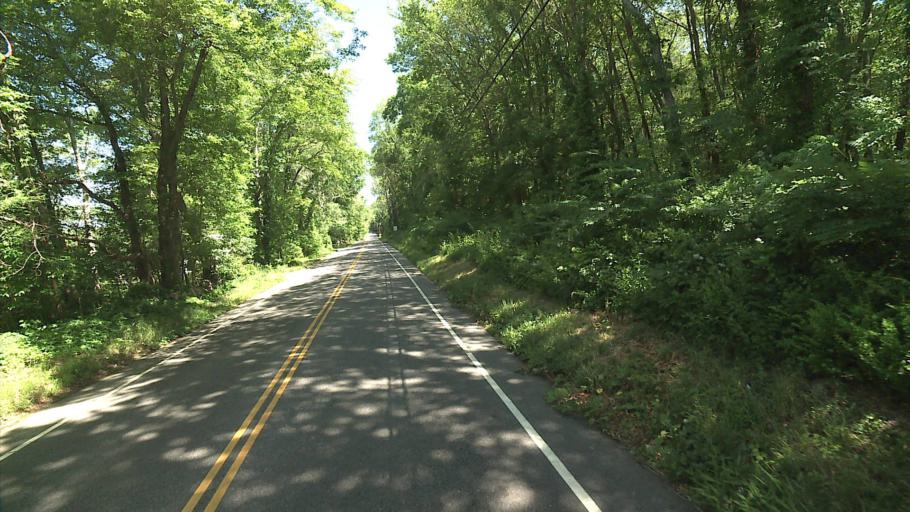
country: US
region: Rhode Island
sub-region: Washington County
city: Hopkinton
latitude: 41.4715
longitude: -71.8323
